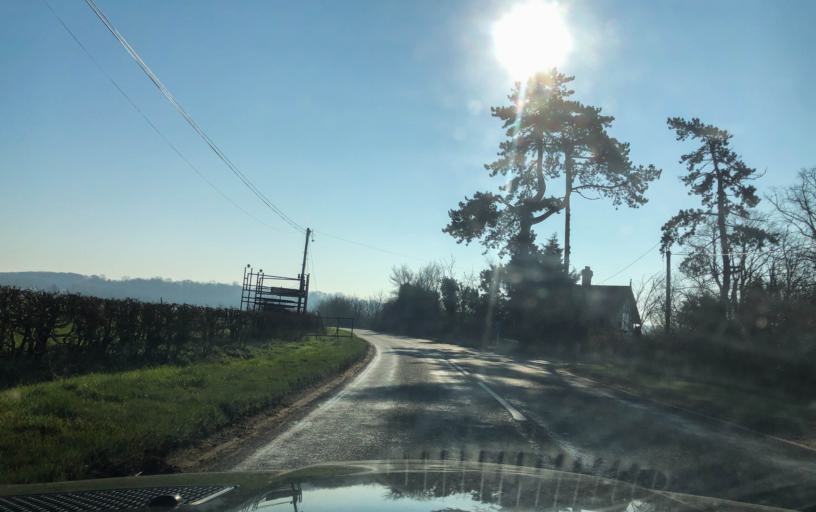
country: GB
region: England
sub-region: Warwickshire
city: Wellesbourne Mountford
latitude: 52.1883
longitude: -1.5825
